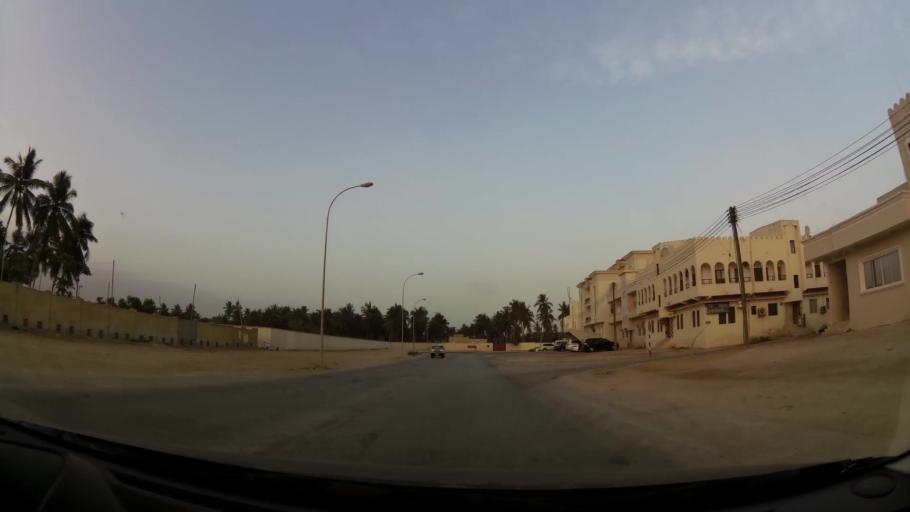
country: OM
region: Zufar
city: Salalah
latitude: 17.0230
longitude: 54.1271
